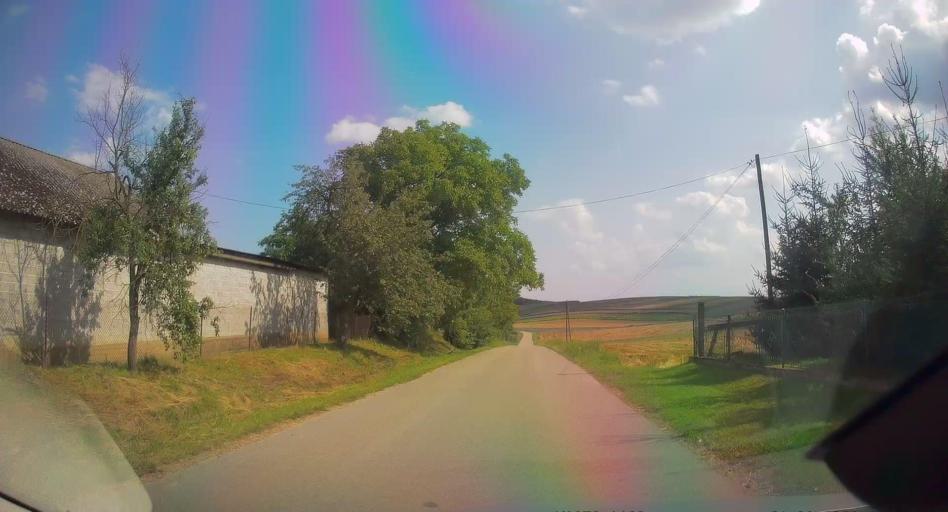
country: PL
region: Lesser Poland Voivodeship
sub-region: Powiat bochenski
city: Dziewin
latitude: 50.1599
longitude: 20.4568
